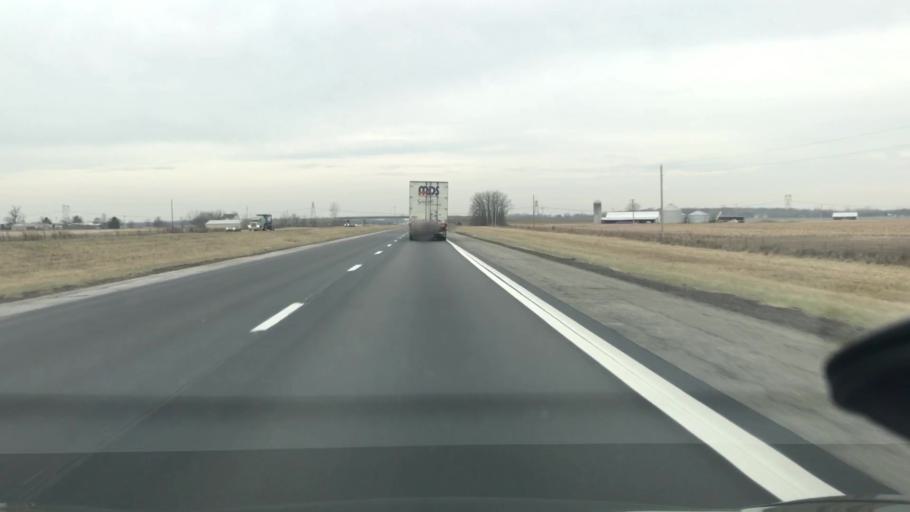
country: US
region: Ohio
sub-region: Madison County
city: Mount Sterling
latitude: 39.7960
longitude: -83.2227
